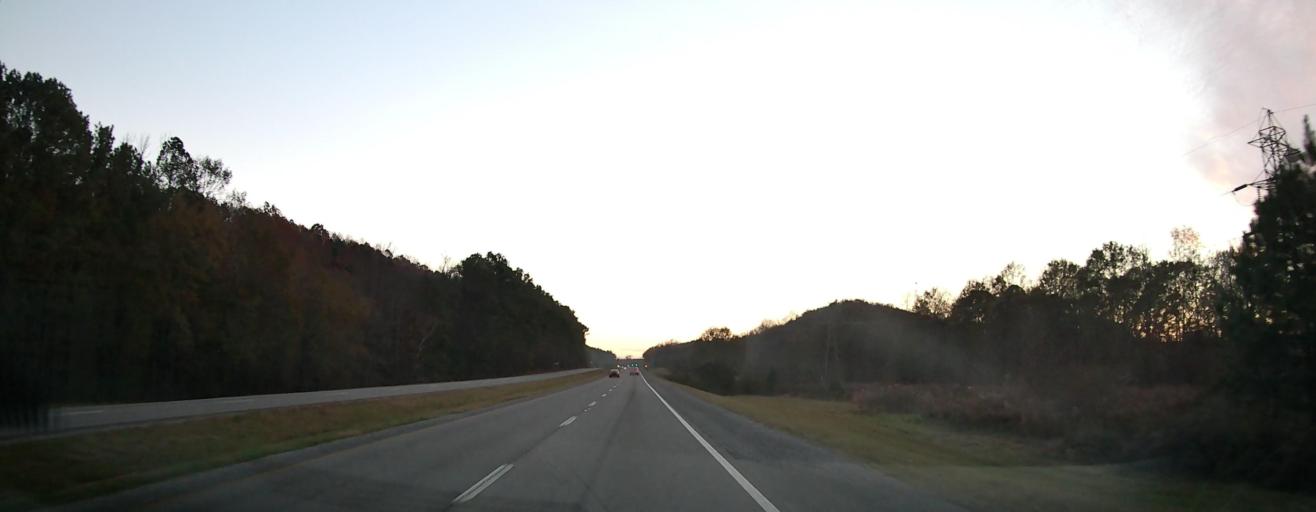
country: US
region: Alabama
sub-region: Calhoun County
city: Alexandria
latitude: 33.8592
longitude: -85.9157
